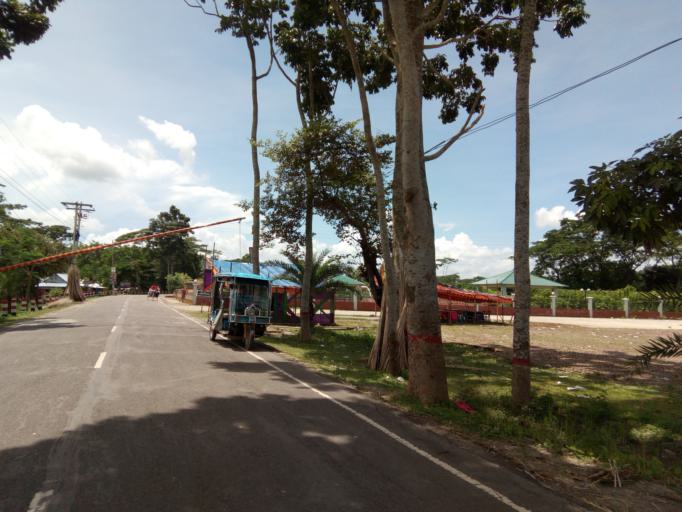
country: BD
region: Dhaka
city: Tungipara
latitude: 22.8984
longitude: 89.8955
